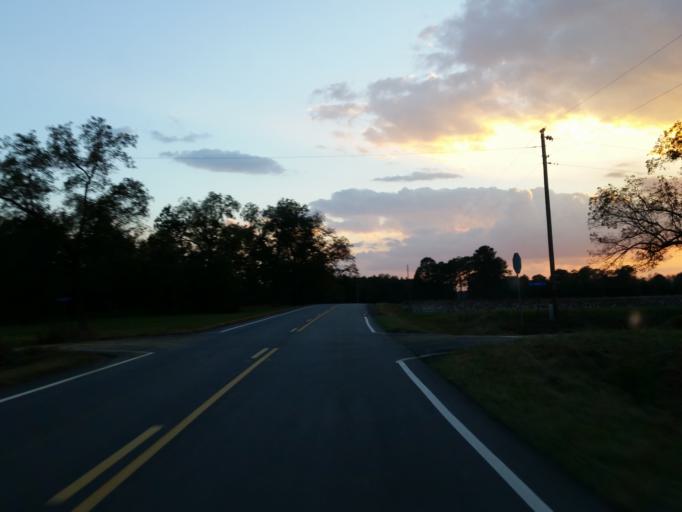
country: US
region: Georgia
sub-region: Pulaski County
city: Hawkinsville
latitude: 32.1795
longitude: -83.5912
